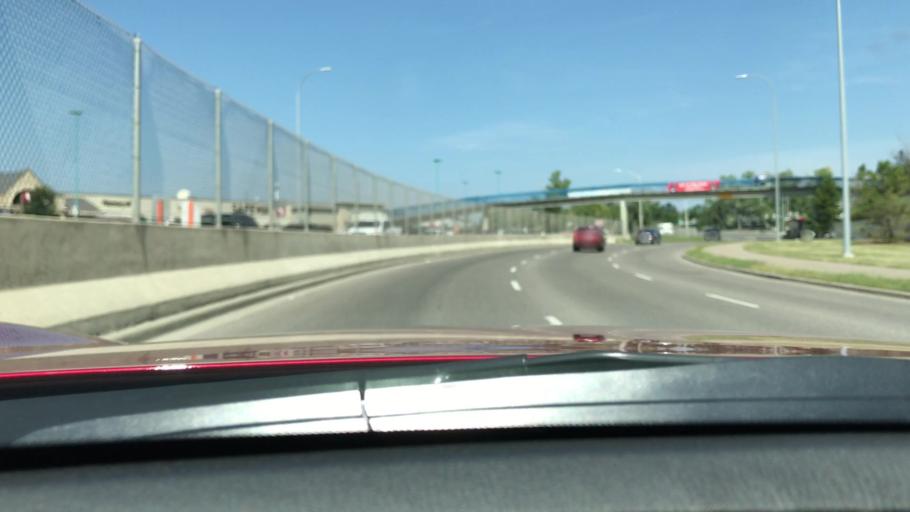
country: CA
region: Alberta
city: Calgary
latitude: 51.0425
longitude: -114.1376
